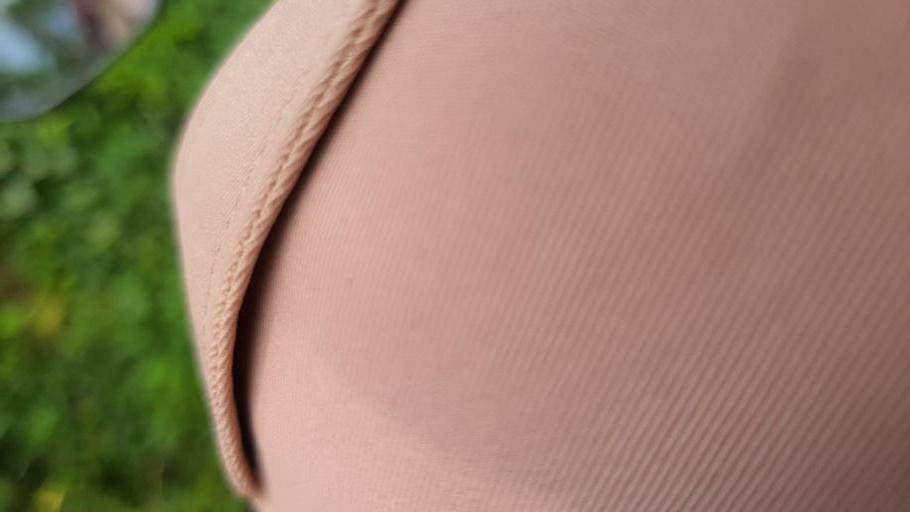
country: ID
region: West Java
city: Caringin
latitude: -6.6451
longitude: 106.8889
